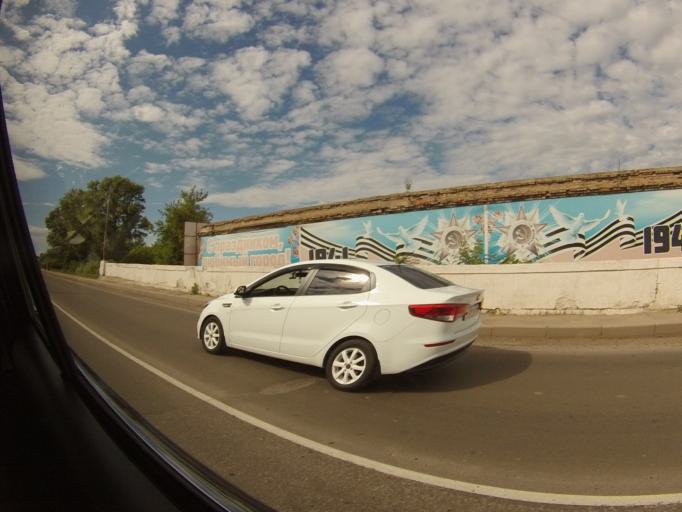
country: RU
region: Orjol
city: Mtsensk
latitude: 53.2821
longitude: 36.5680
